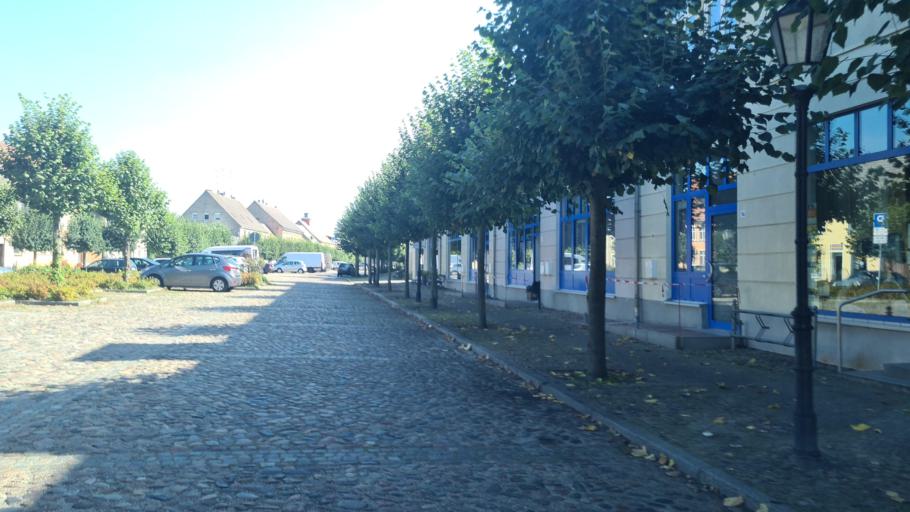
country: DE
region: Brandenburg
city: Friesack
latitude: 52.7420
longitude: 12.5794
